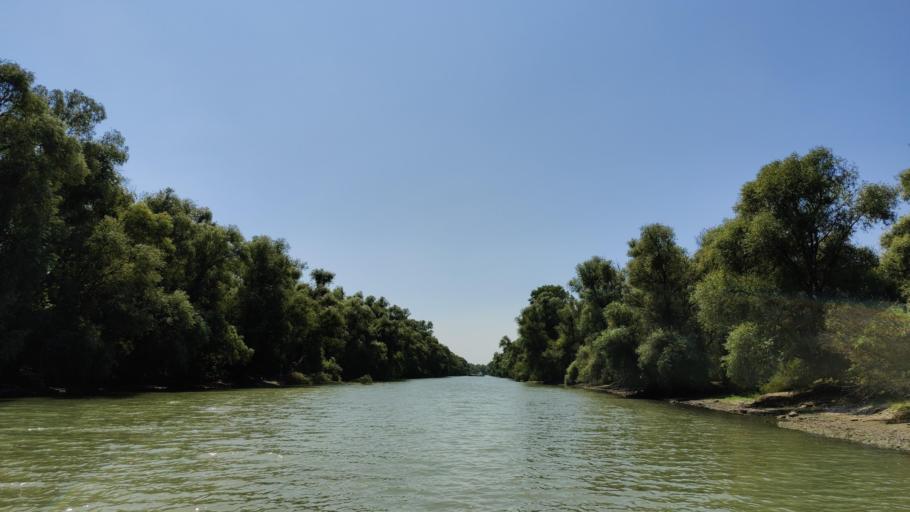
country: RO
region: Tulcea
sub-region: Comuna Pardina
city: Pardina
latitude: 45.2492
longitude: 28.9242
